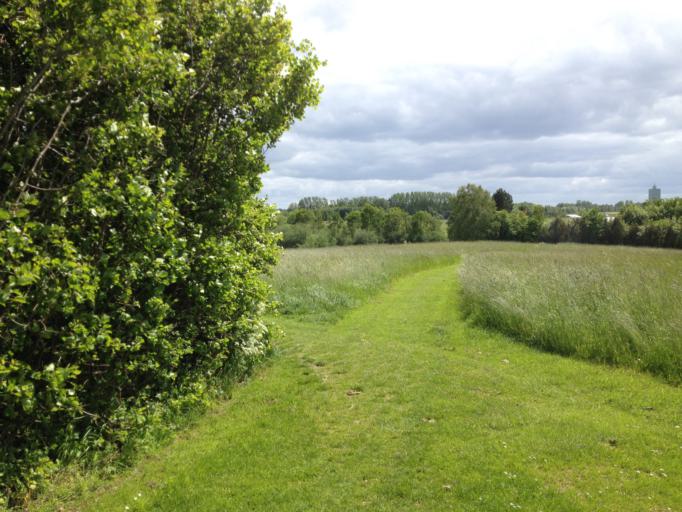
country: DK
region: Capital Region
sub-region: Fredensborg Kommune
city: Niva
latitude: 55.9323
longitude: 12.4859
